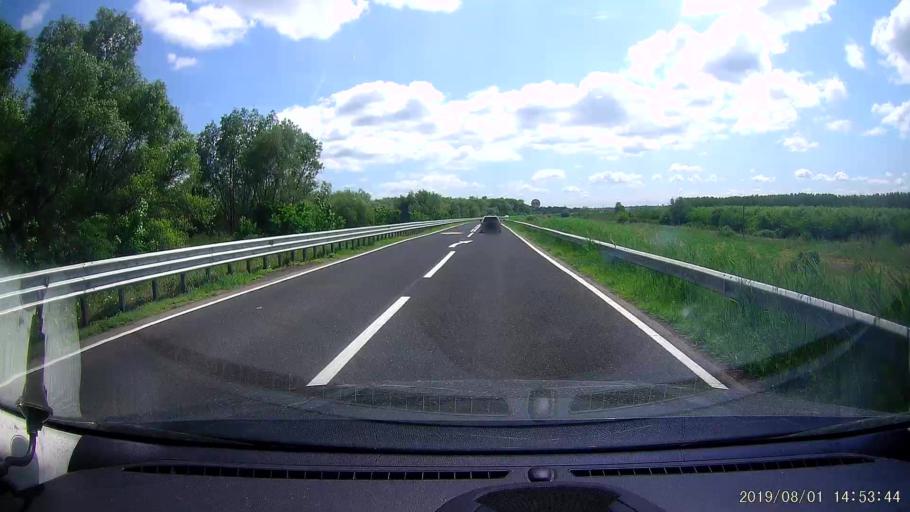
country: RO
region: Braila
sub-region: Municipiul Braila
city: Braila
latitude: 45.3292
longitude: 27.9988
